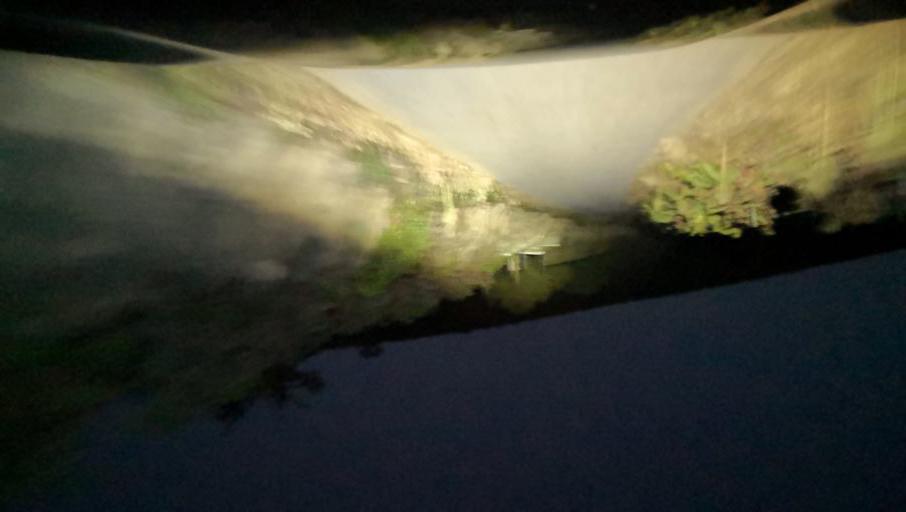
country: PT
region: Viseu
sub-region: Armamar
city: Armamar
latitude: 41.1572
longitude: -7.6985
